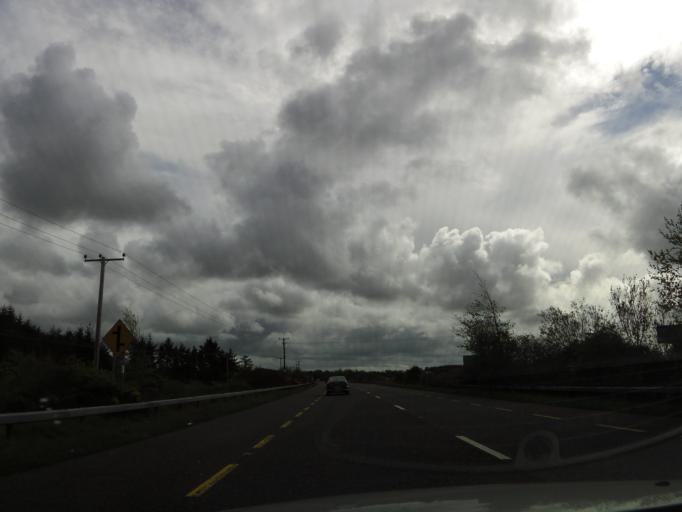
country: IE
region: Connaught
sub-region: Maigh Eo
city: Claremorris
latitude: 53.7157
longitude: -8.9859
